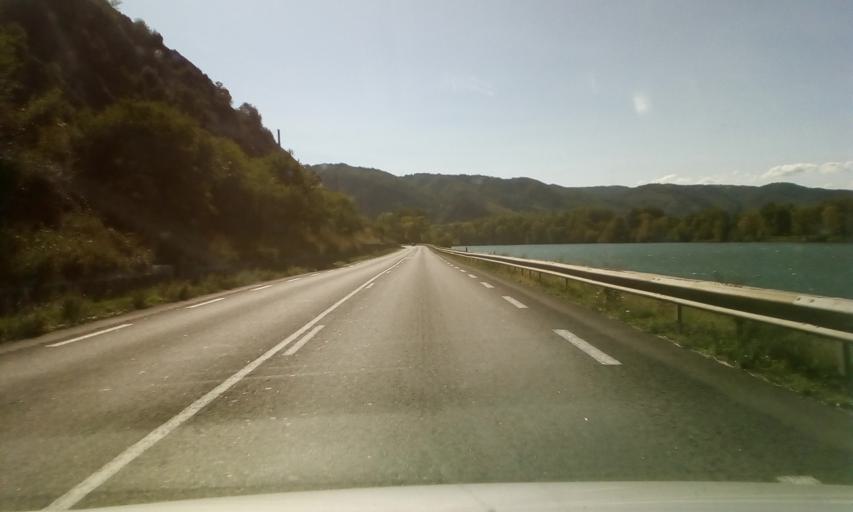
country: FR
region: Rhone-Alpes
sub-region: Departement de l'Ardeche
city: Tournon-sur-Rhone
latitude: 45.0847
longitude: 4.8321
